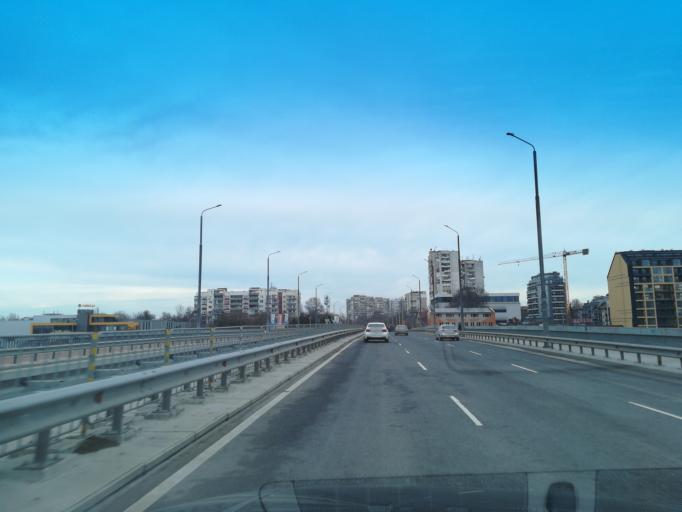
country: BG
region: Plovdiv
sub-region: Obshtina Plovdiv
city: Plovdiv
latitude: 42.1530
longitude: 24.7312
